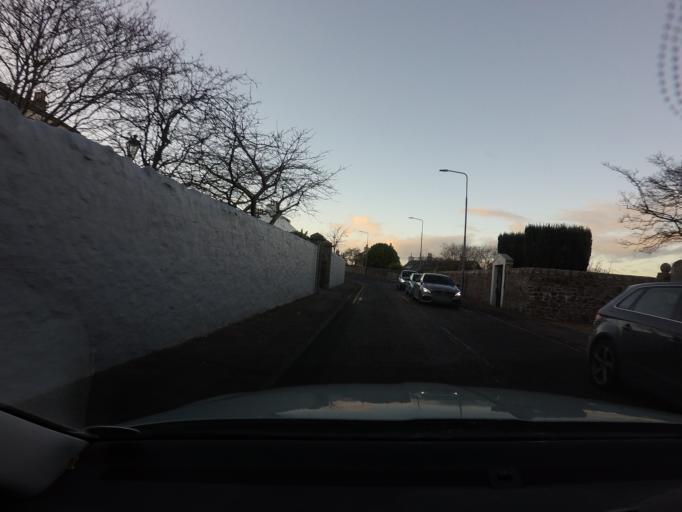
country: GB
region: Scotland
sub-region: Fife
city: Tayport
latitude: 56.4512
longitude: -2.8850
